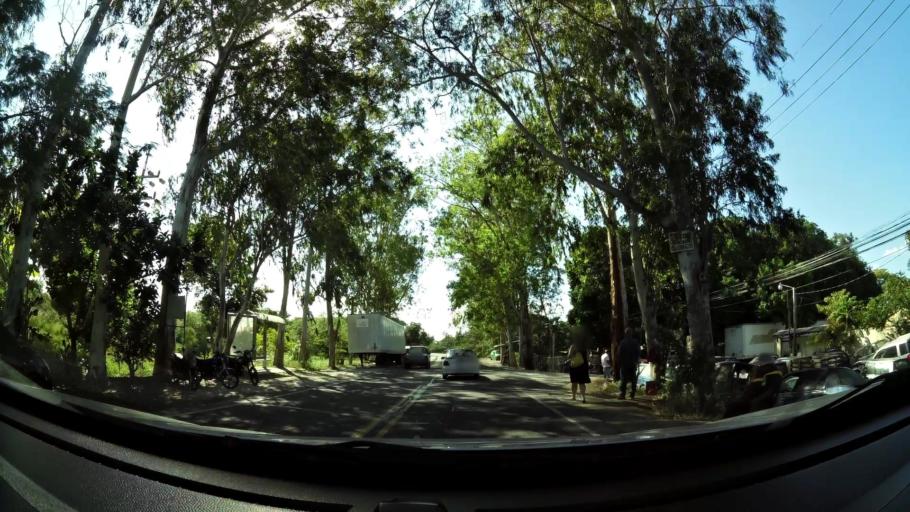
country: CR
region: Guanacaste
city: Liberia
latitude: 10.6124
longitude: -85.4947
